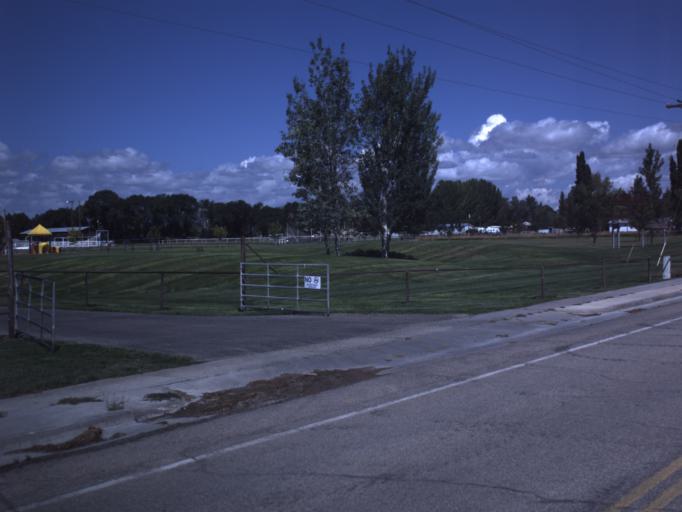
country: US
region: Utah
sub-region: Duchesne County
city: Roosevelt
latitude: 40.4288
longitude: -110.0300
